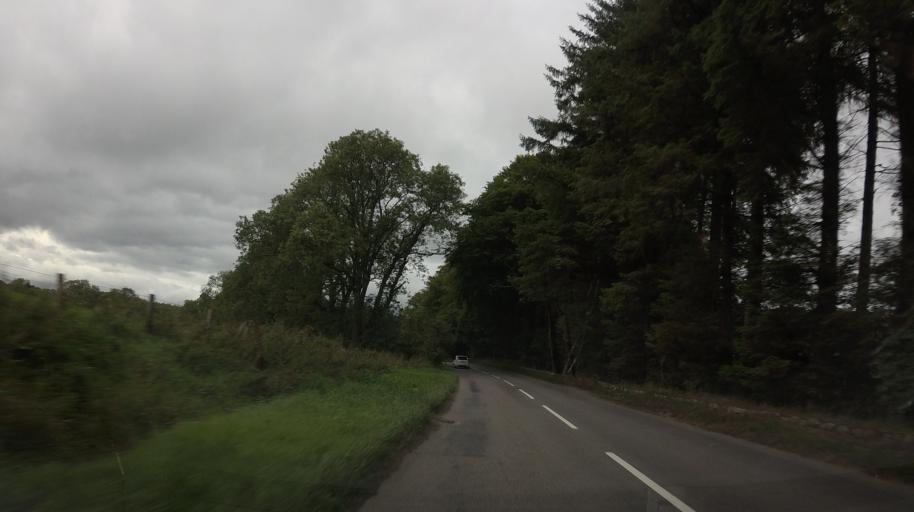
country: GB
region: Scotland
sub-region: Aberdeenshire
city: Kemnay
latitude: 57.1555
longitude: -2.4308
